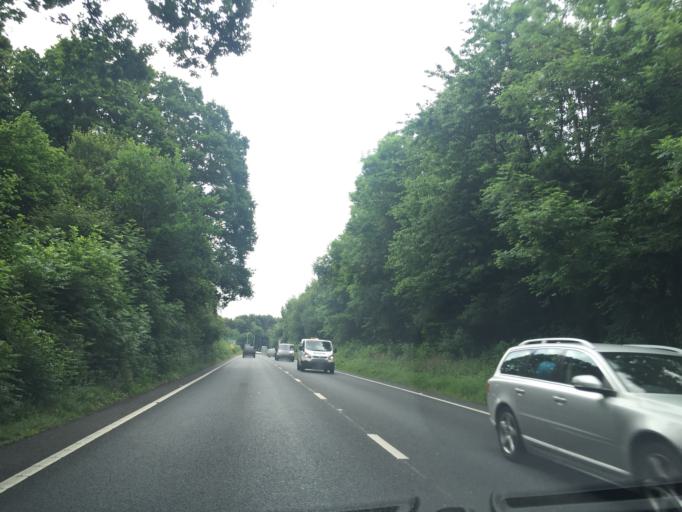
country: GB
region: England
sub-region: Dorset
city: Wimborne Minster
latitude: 50.7881
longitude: -1.9833
